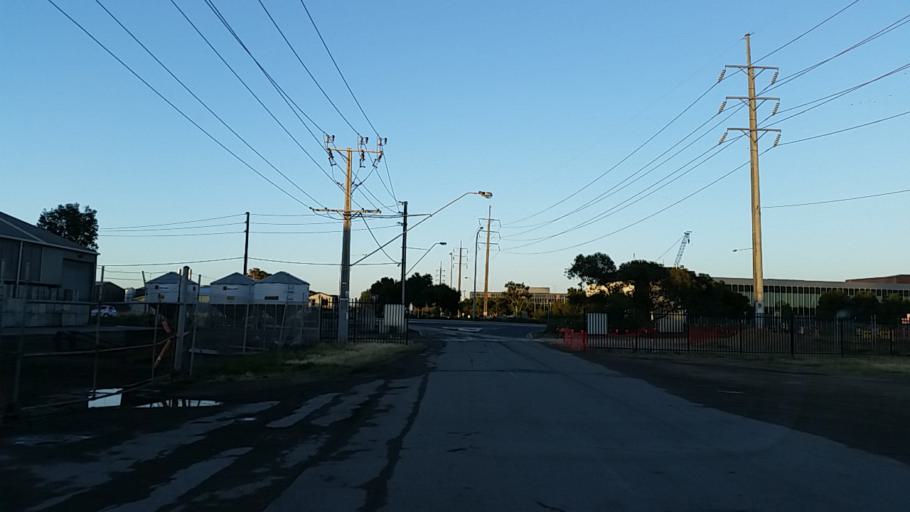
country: AU
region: South Australia
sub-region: Port Adelaide Enfield
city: Birkenhead
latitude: -34.7909
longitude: 138.5057
